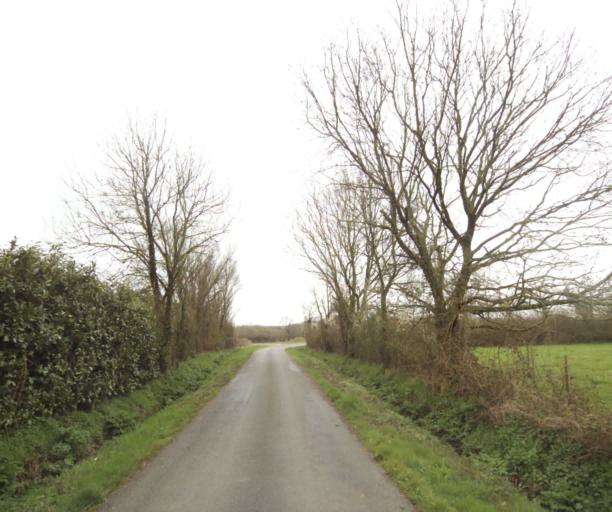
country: FR
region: Pays de la Loire
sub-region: Departement de la Loire-Atlantique
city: Bouvron
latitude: 47.4383
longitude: -1.8820
